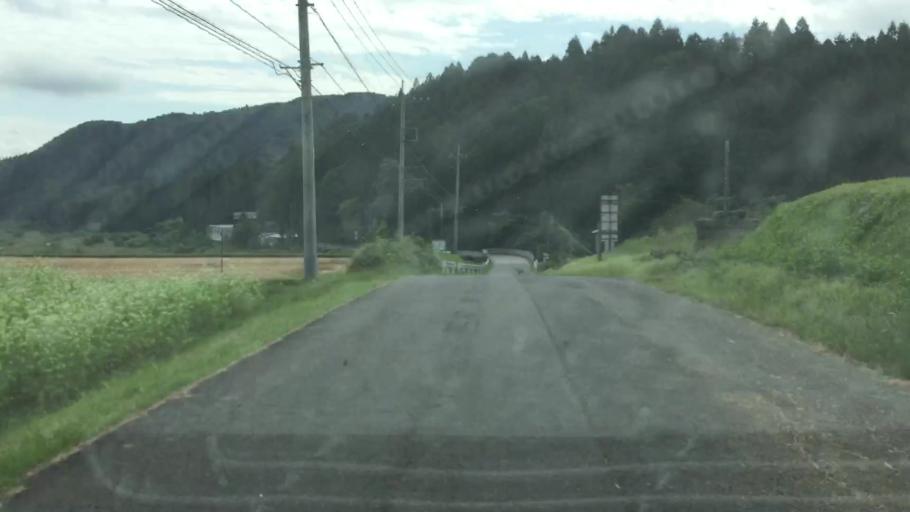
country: JP
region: Tochigi
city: Imaichi
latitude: 36.7640
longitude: 139.6765
